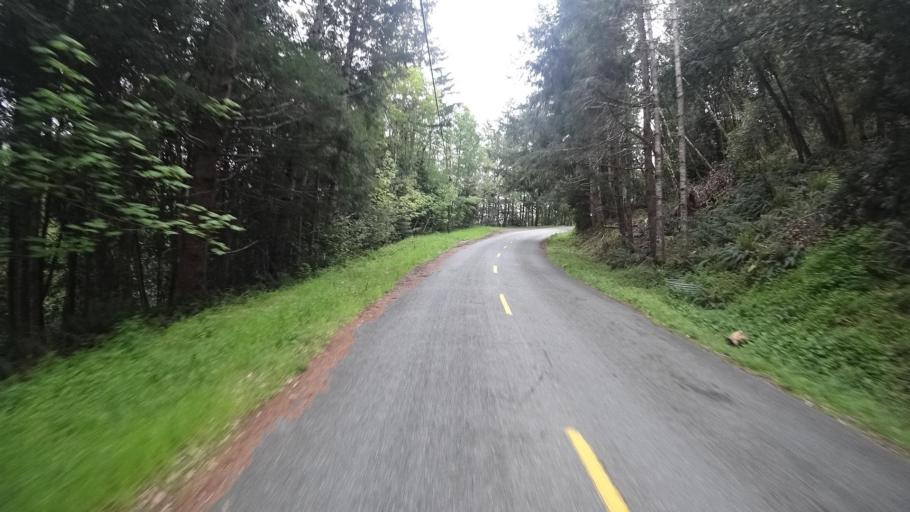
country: US
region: California
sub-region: Humboldt County
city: Blue Lake
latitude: 40.9456
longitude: -123.8427
